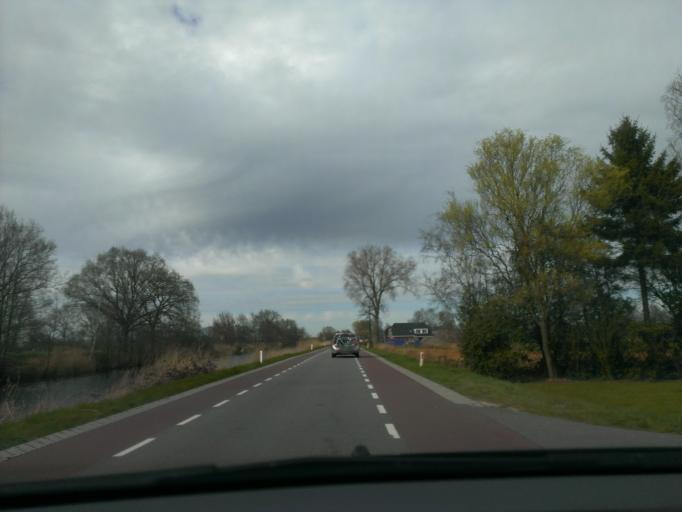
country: NL
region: Gelderland
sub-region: Gemeente Epe
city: Vaassen
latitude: 52.2490
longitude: 5.9795
